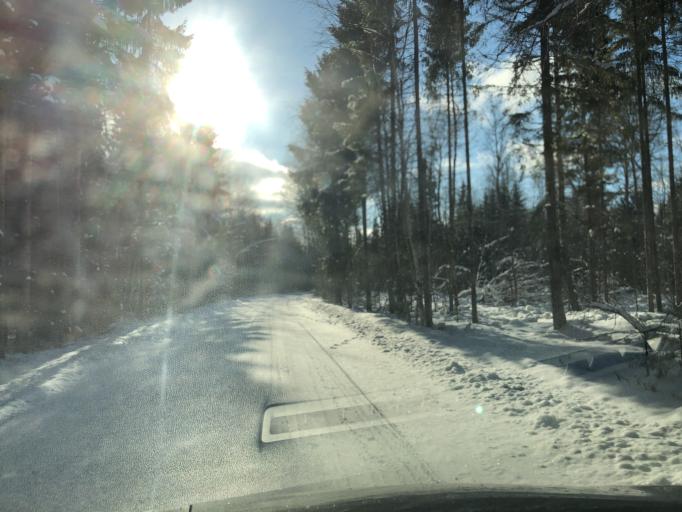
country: EE
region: Jaervamaa
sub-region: Paide linn
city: Paide
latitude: 59.0464
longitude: 25.4782
